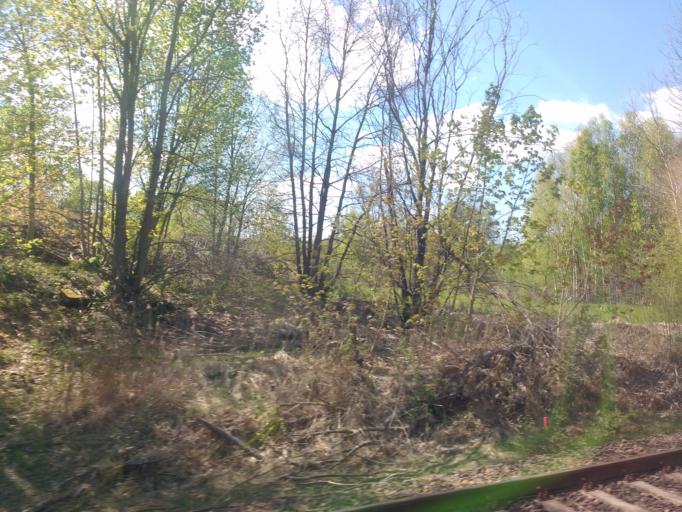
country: DE
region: Berlin
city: Grunau
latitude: 52.4165
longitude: 13.5664
